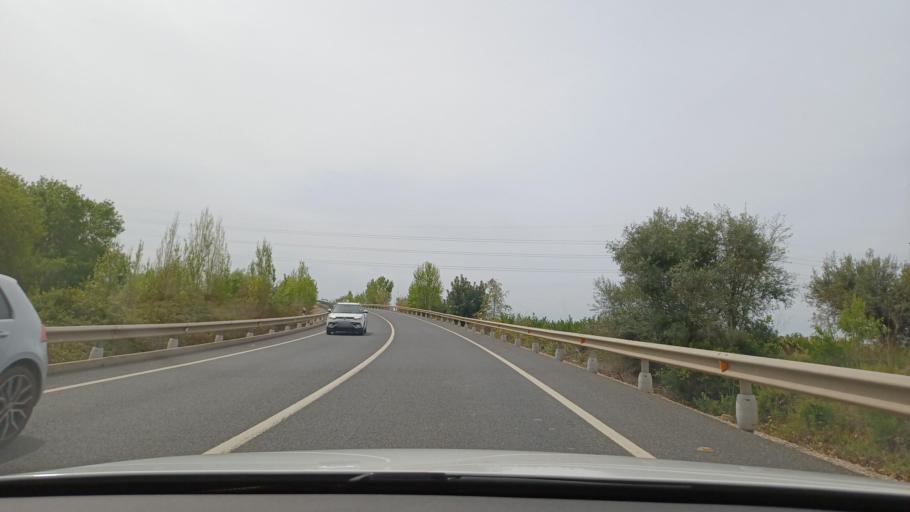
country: ES
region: Catalonia
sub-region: Provincia de Tarragona
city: la Pobla de Mafumet
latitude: 41.1974
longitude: 1.2427
